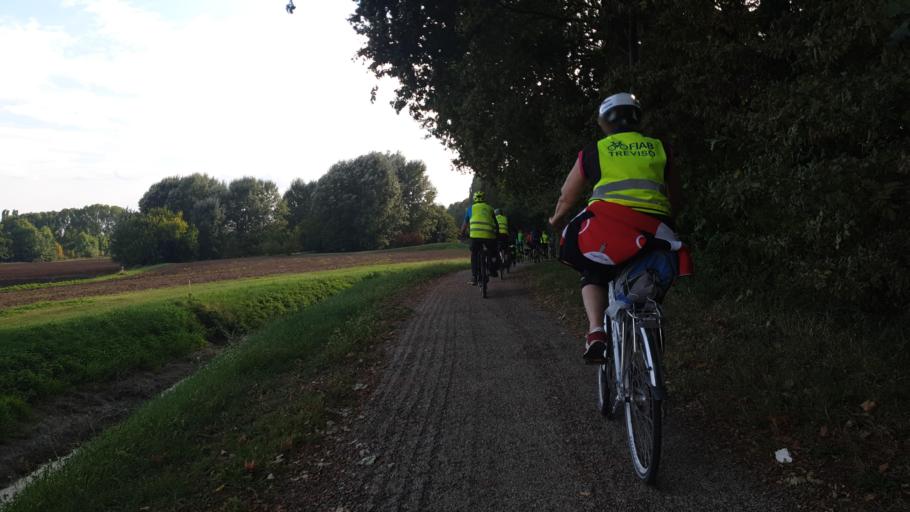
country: IT
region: Veneto
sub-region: Provincia di Padova
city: Montagnana
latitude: 45.2474
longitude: 11.4728
